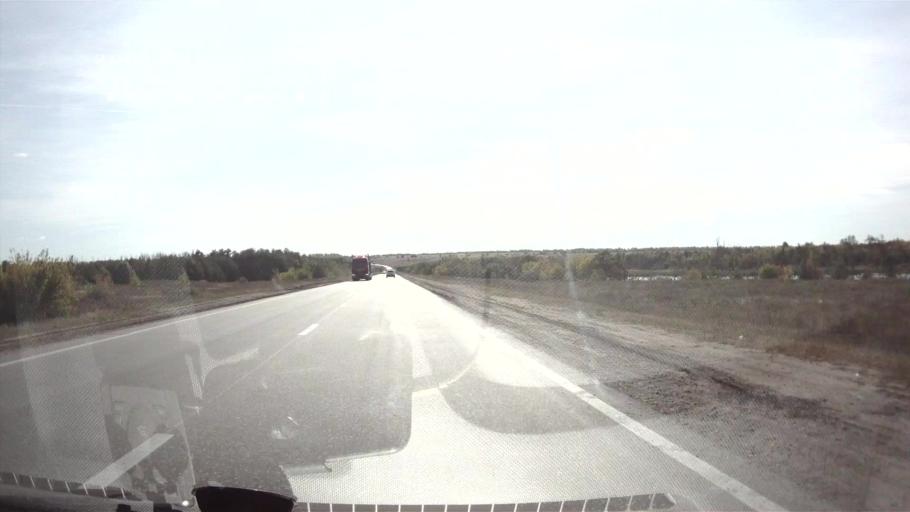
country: RU
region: Samara
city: Varlamovo
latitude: 53.1419
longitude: 48.2845
